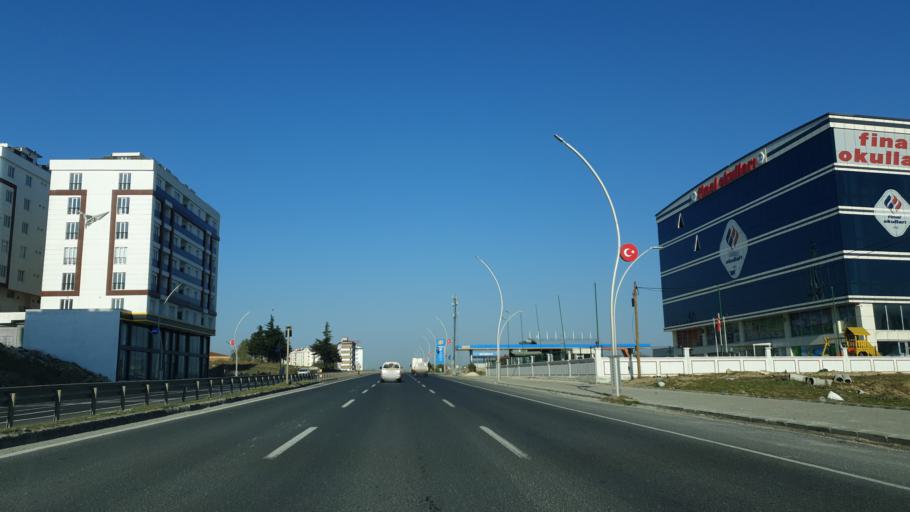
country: TR
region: Tekirdag
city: Cerkezkoey
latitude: 41.2732
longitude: 27.9755
